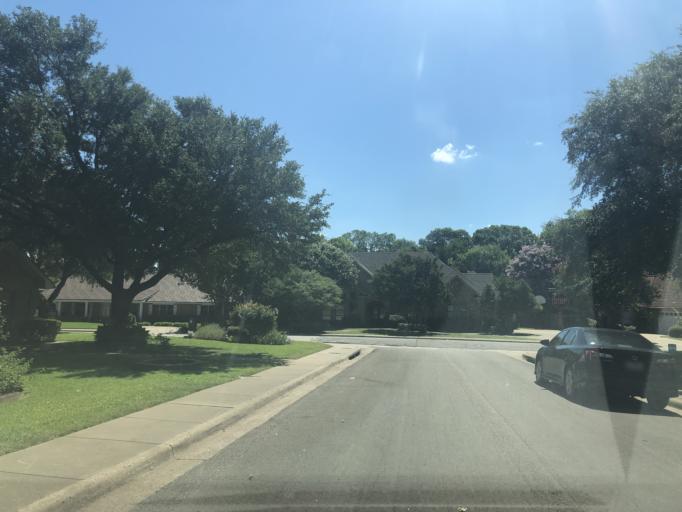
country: US
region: Texas
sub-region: Dallas County
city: Duncanville
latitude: 32.6468
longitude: -96.9295
